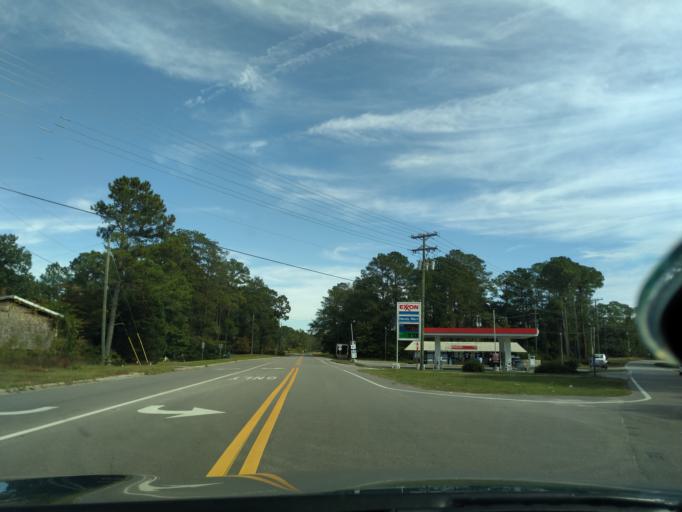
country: US
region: North Carolina
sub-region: Beaufort County
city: River Road
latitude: 35.5040
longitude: -76.9875
